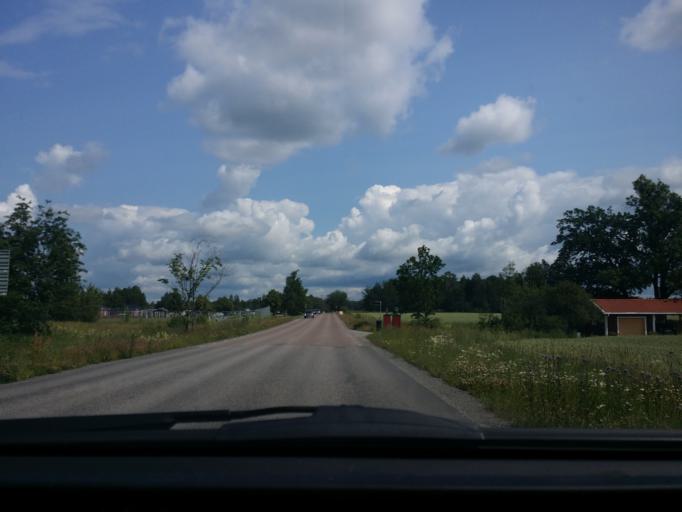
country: SE
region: Vaestmanland
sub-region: Vasteras
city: Hokasen
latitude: 59.6193
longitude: 16.6221
